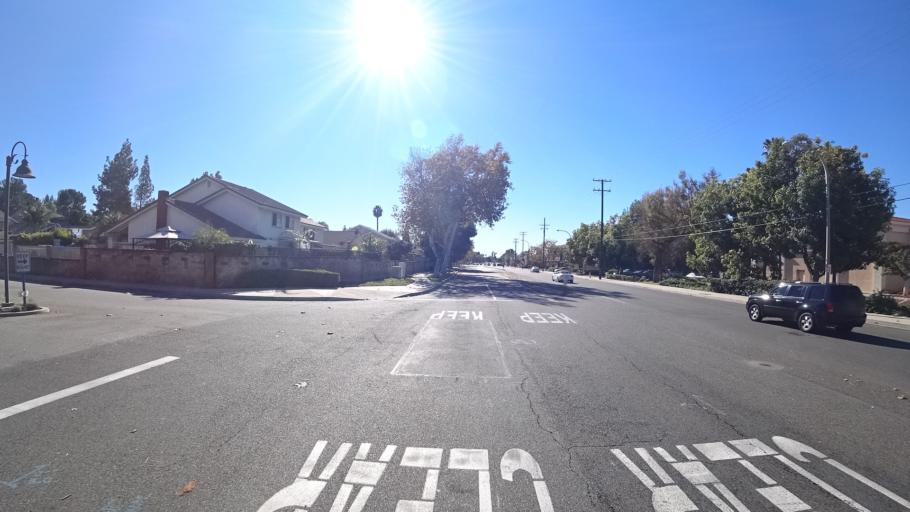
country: US
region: California
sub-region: Orange County
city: Brea
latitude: 33.9343
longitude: -117.8932
